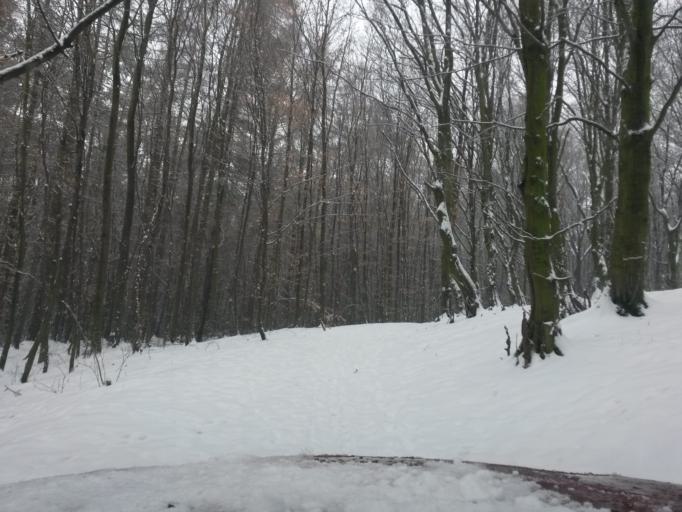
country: SK
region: Kosicky
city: Kosice
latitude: 48.7220
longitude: 21.3073
